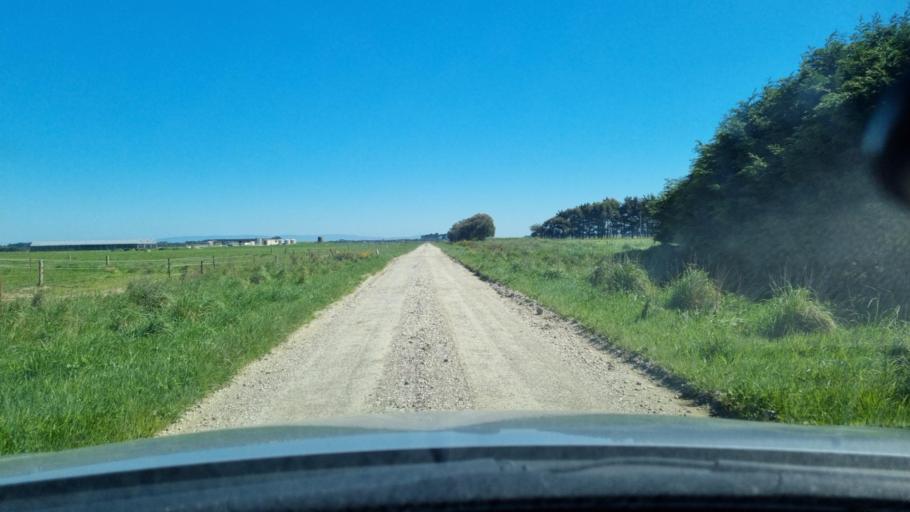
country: NZ
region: Southland
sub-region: Invercargill City
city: Invercargill
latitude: -46.4238
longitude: 168.3147
